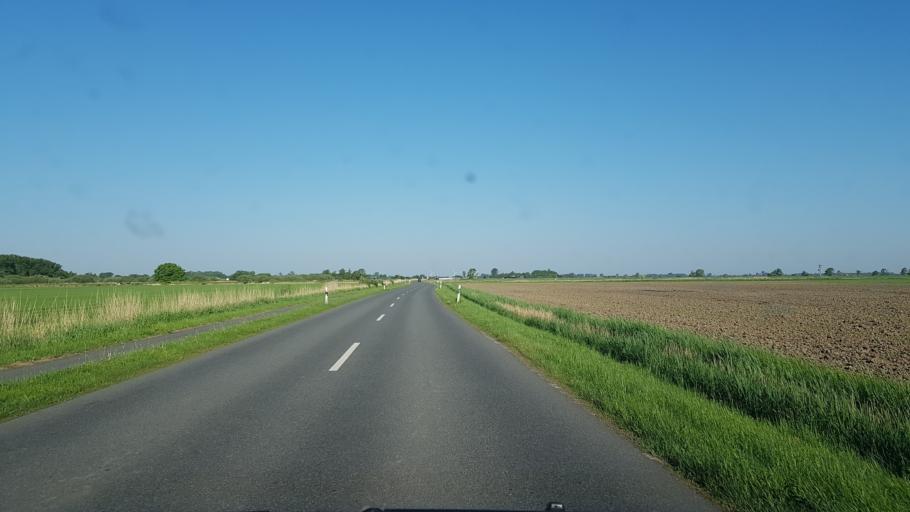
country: DE
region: Lower Saxony
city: Langen
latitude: 53.6117
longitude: 8.5669
